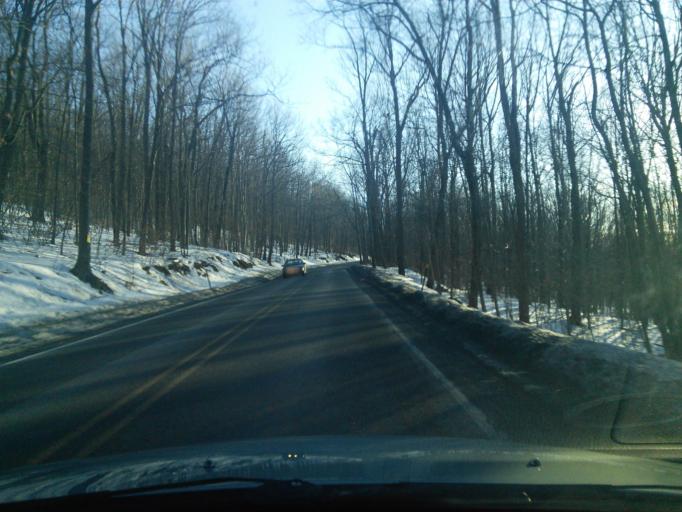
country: US
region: Pennsylvania
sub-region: Centre County
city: Park Forest Village
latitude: 40.8538
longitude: -77.9390
